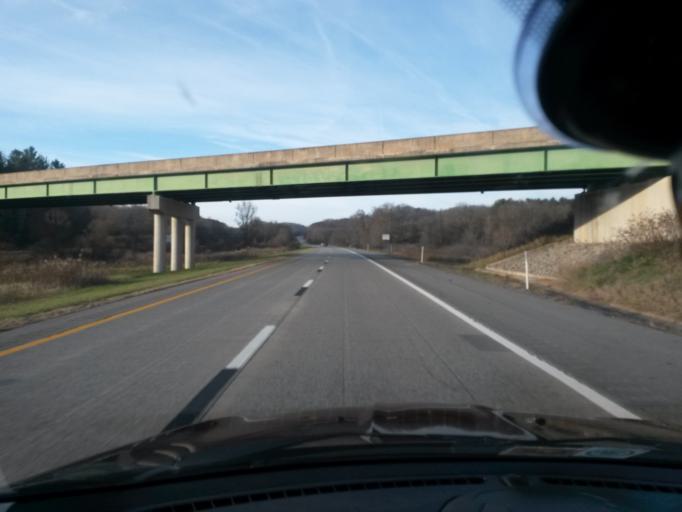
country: US
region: West Virginia
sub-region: Greenbrier County
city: Rainelle
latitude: 37.8983
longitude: -80.6505
